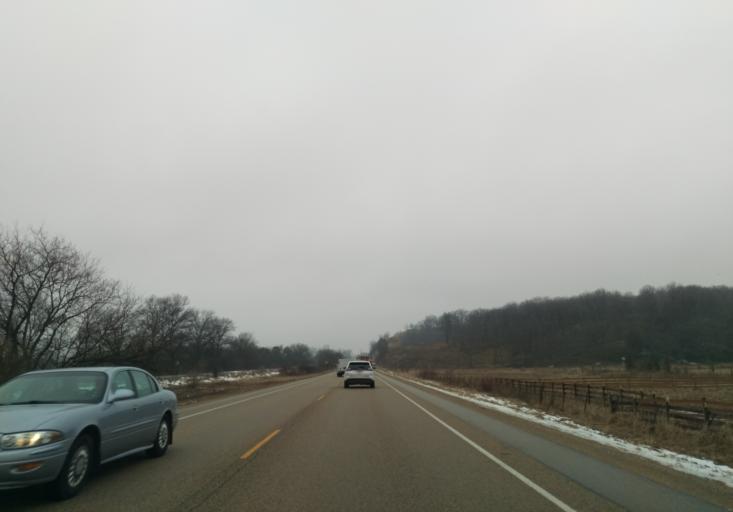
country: US
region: Wisconsin
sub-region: Dane County
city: Cross Plains
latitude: 43.1175
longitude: -89.6783
